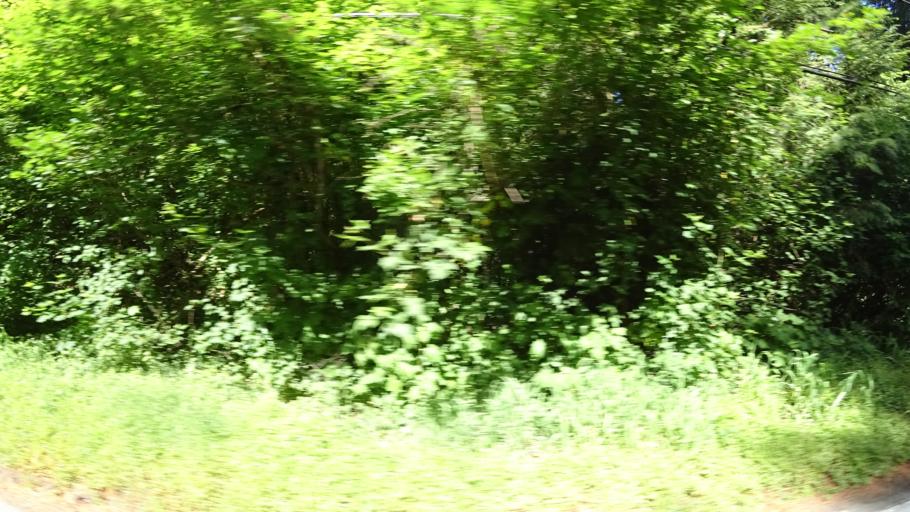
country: US
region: Oregon
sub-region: Washington County
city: Oak Hills
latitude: 45.5840
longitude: -122.8016
